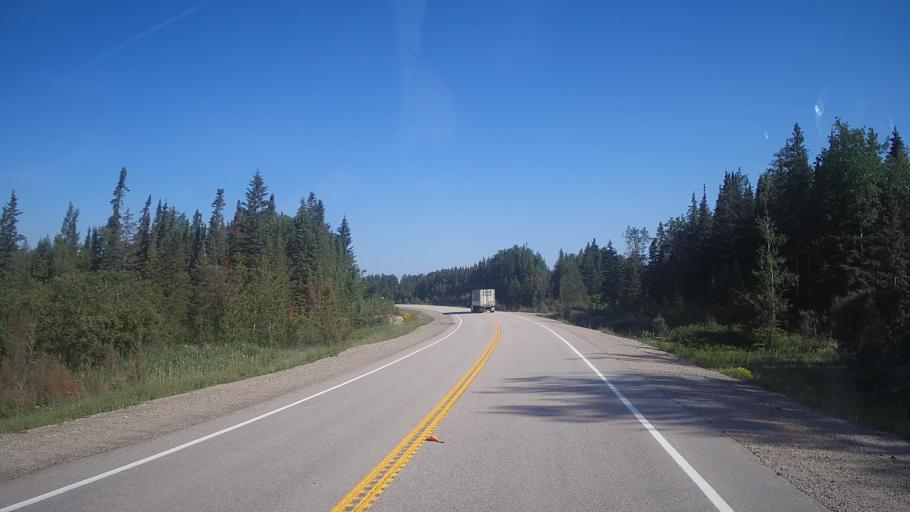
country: CA
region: Ontario
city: Dryden
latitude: 49.5825
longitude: -92.2631
